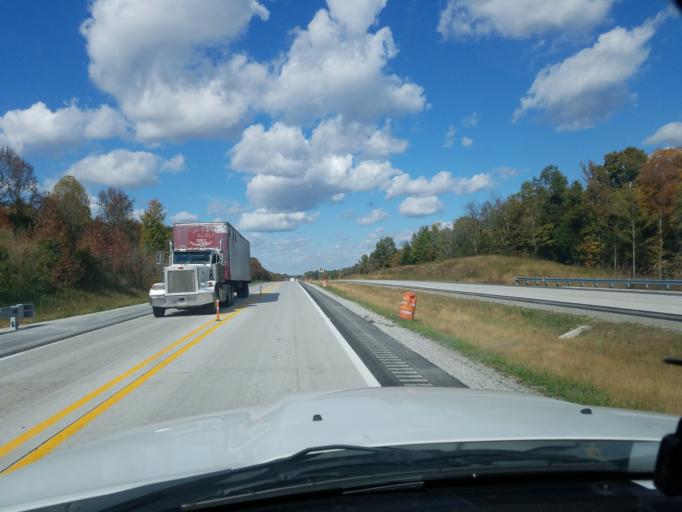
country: US
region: Kentucky
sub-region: Ohio County
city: Beaver Dam
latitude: 37.3966
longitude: -86.8176
